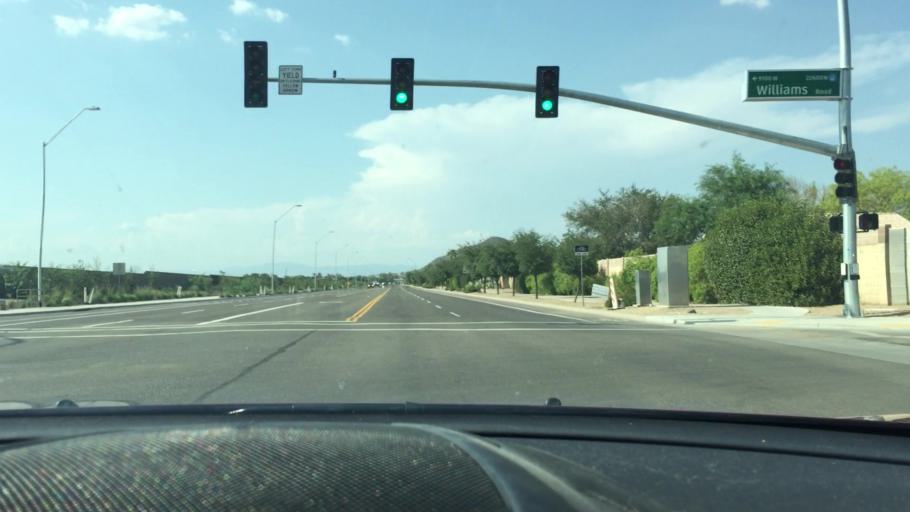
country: US
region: Arizona
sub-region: Maricopa County
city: Sun City West
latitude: 33.6891
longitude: -112.2551
